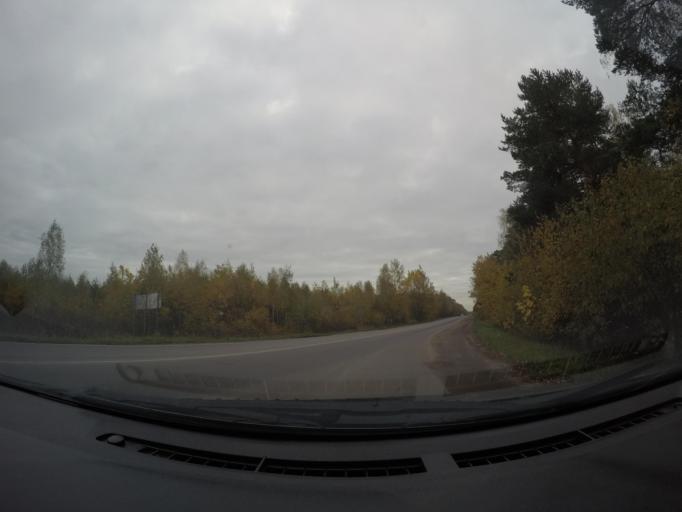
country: RU
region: Moskovskaya
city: Obukhovo
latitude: 55.7812
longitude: 38.2485
